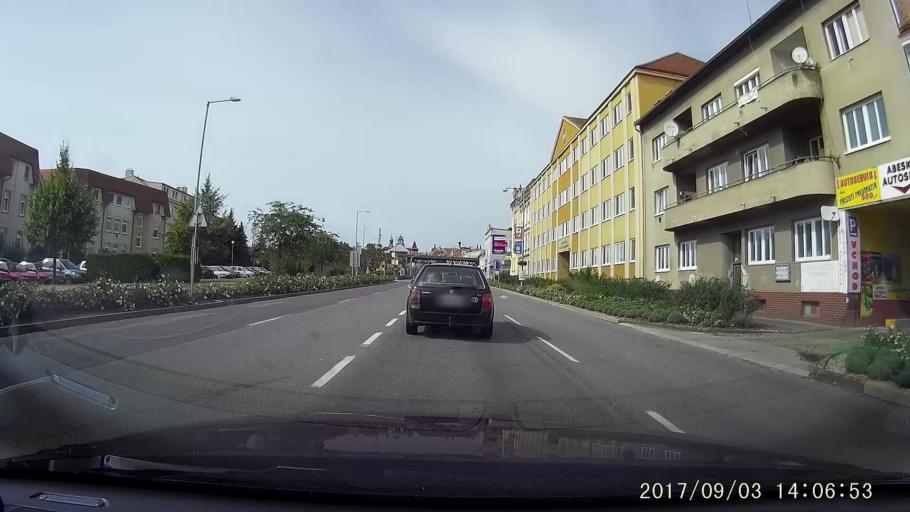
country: CZ
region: South Moravian
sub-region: Okres Znojmo
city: Znojmo
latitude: 48.8484
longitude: 16.0561
